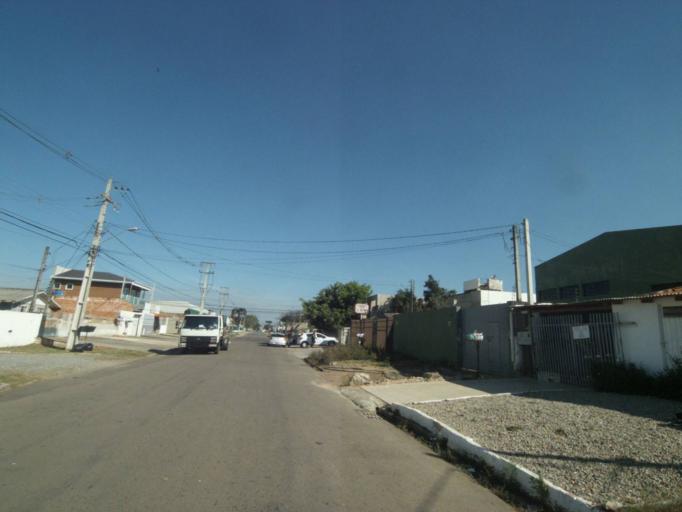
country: BR
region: Parana
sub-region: Sao Jose Dos Pinhais
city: Sao Jose dos Pinhais
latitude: -25.4905
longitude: -49.2347
